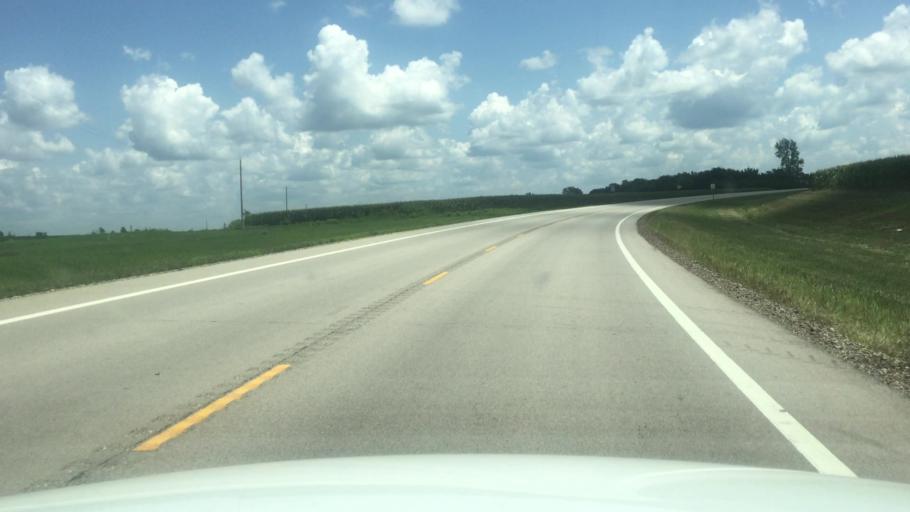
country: US
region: Kansas
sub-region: Brown County
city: Horton
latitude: 39.6672
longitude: -95.4218
